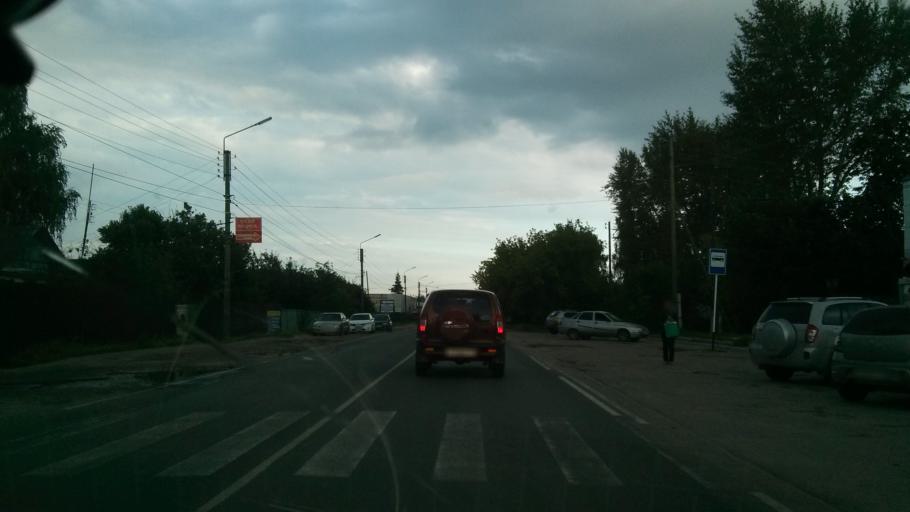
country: RU
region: Vladimir
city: Murom
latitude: 55.5928
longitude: 42.0348
